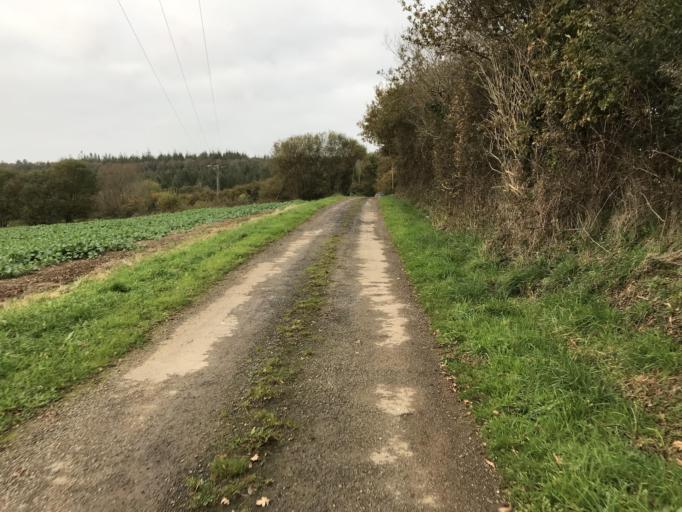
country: FR
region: Brittany
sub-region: Departement du Finistere
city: Hopital-Camfrout
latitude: 48.3240
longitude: -4.2143
